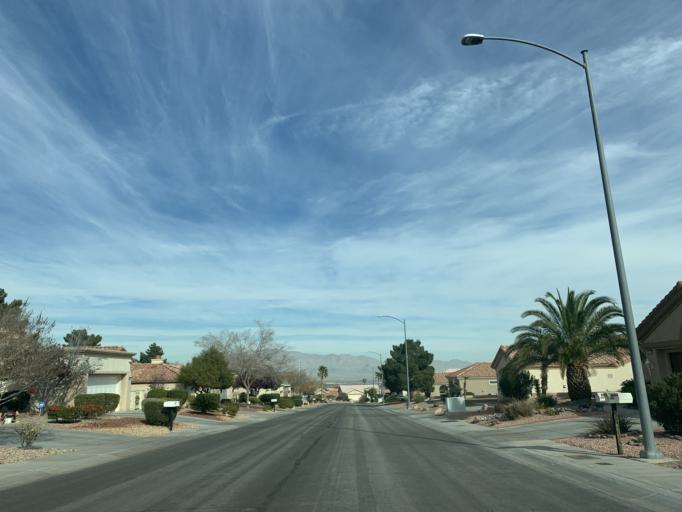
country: US
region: Nevada
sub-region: Clark County
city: Summerlin South
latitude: 36.2156
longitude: -115.3295
